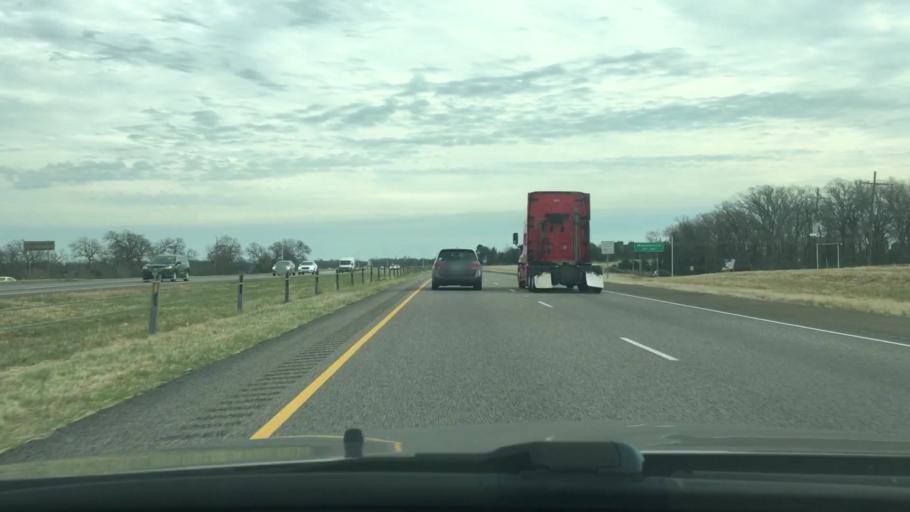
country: US
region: Texas
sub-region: Madison County
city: Madisonville
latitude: 30.9626
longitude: -95.8800
